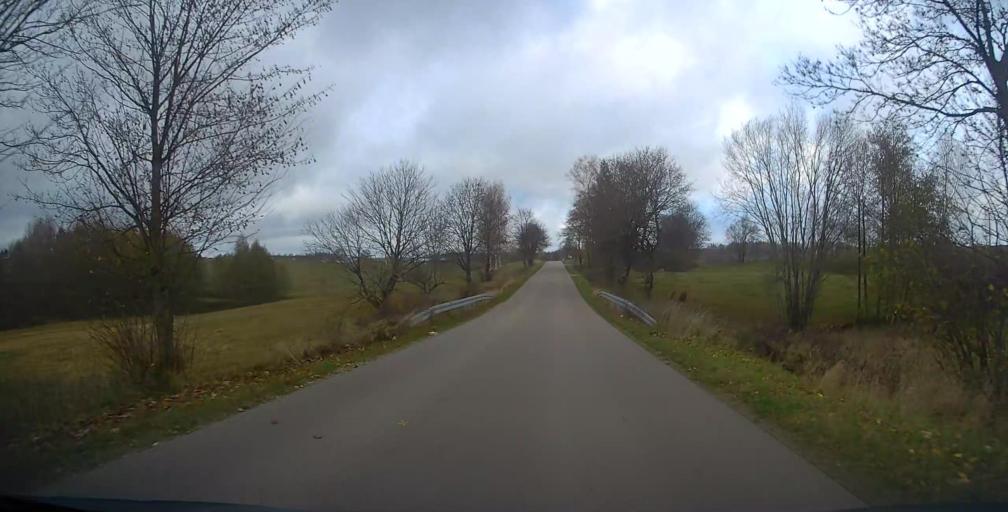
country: PL
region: Podlasie
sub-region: Suwalki
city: Suwalki
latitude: 54.3213
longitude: 22.8630
